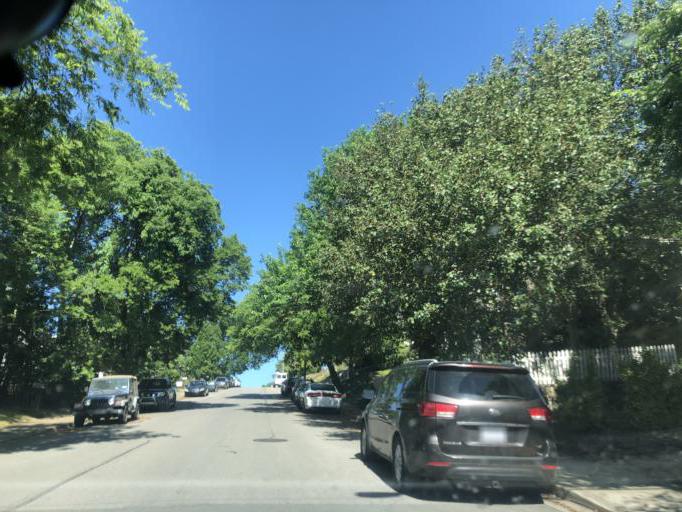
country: US
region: Tennessee
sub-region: Davidson County
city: Nashville
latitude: 36.1289
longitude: -86.7902
